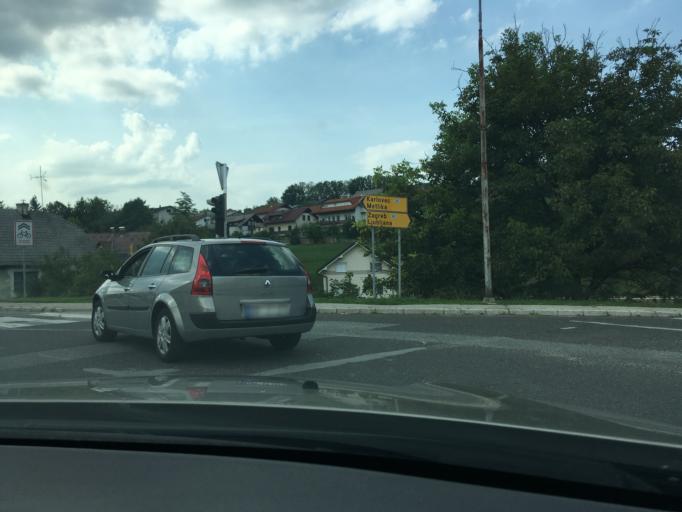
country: SI
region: Novo Mesto
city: Novo Mesto
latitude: 45.7996
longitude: 15.1800
